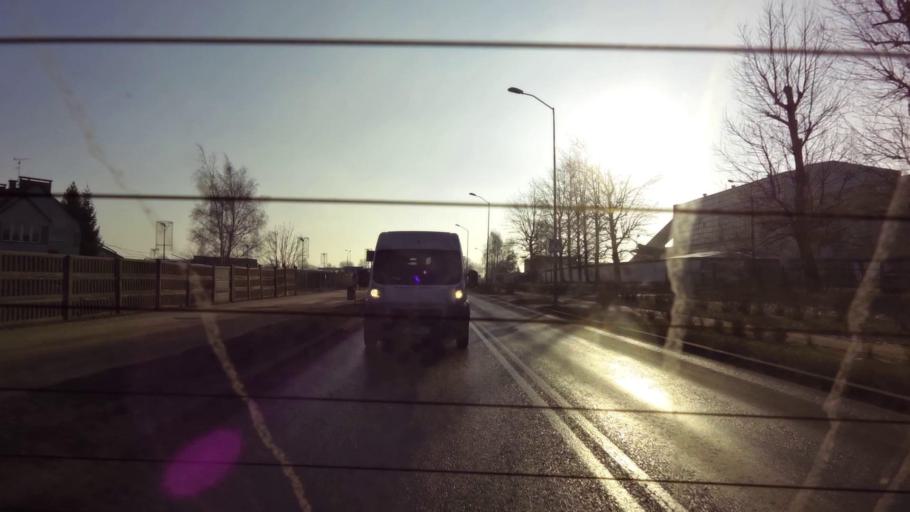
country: PL
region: West Pomeranian Voivodeship
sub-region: Koszalin
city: Koszalin
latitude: 54.1763
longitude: 16.1740
